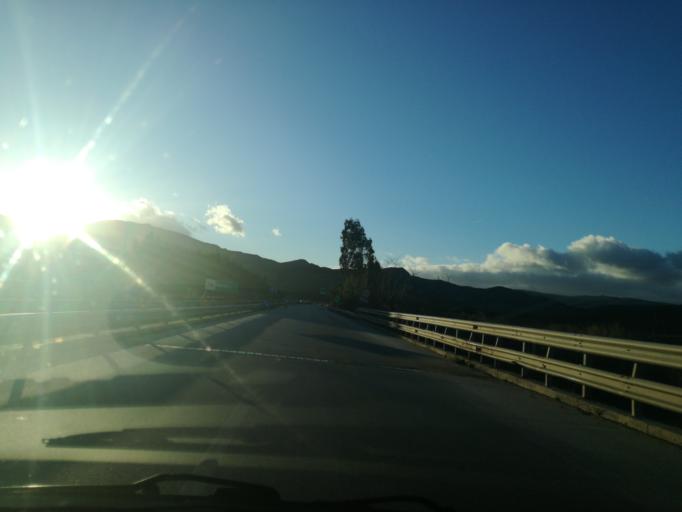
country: IT
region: Sicily
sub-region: Palermo
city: Castellana Sicula
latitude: 37.7440
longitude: 13.9847
